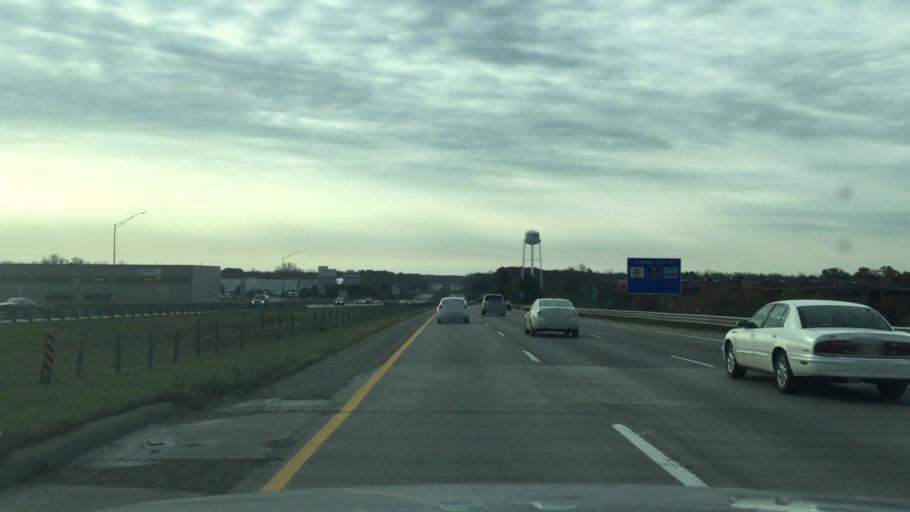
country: US
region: Michigan
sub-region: Wayne County
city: Plymouth
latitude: 42.3808
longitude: -83.4371
